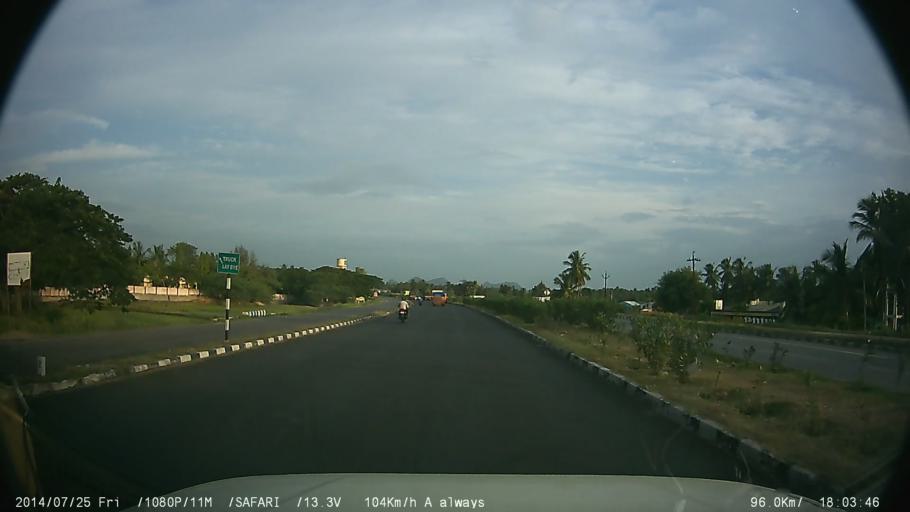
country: IN
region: Tamil Nadu
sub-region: Krishnagiri
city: Kaverippattanam
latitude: 12.4575
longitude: 78.2156
